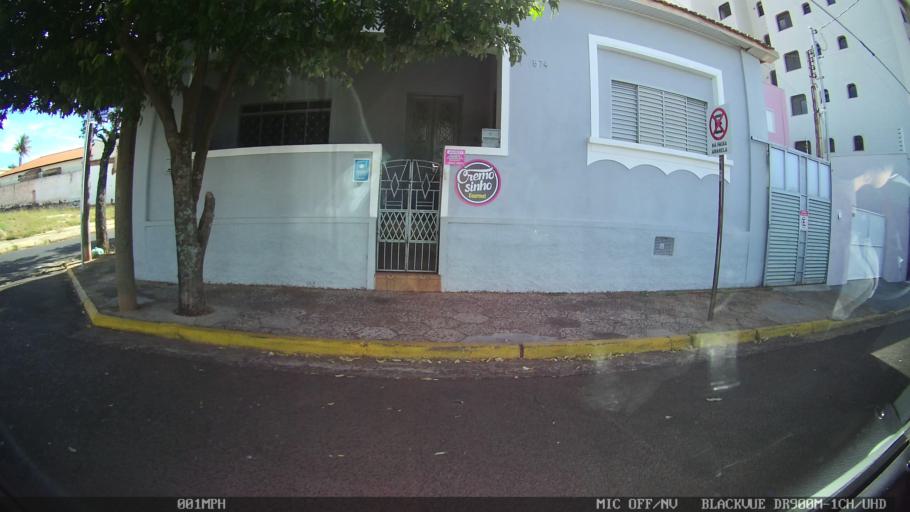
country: BR
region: Sao Paulo
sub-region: Catanduva
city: Catanduva
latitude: -21.1265
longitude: -48.9698
